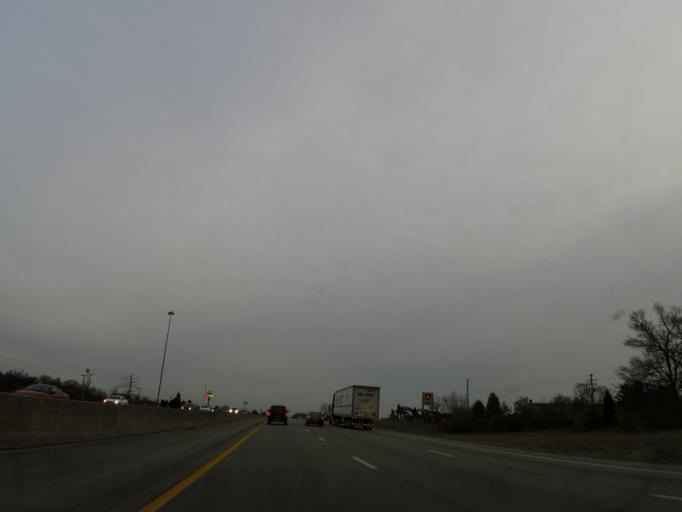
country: US
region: Kentucky
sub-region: Madison County
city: Richmond
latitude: 37.8487
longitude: -84.3299
